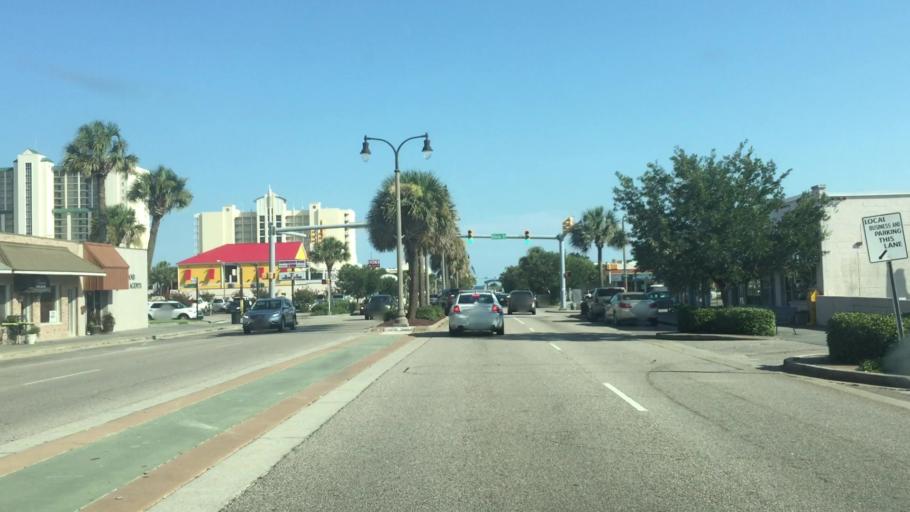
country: US
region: South Carolina
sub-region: Horry County
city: North Myrtle Beach
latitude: 33.8211
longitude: -78.6737
